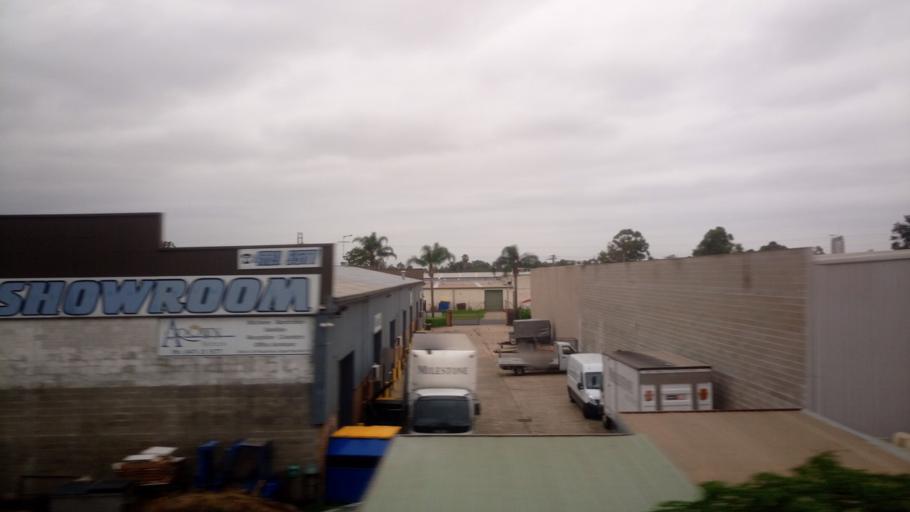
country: AU
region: New South Wales
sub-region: Penrith Municipality
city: Penrith
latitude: -33.7482
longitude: 150.6876
